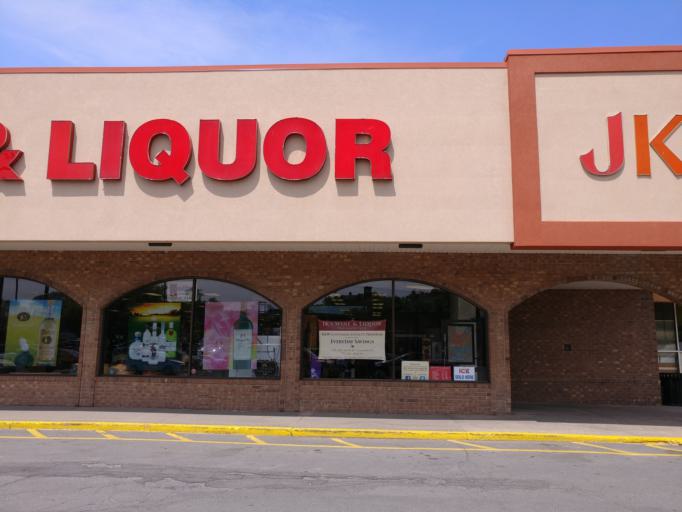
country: US
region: New York
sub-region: Ulster County
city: Kingston
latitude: 41.9375
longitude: -74.0185
